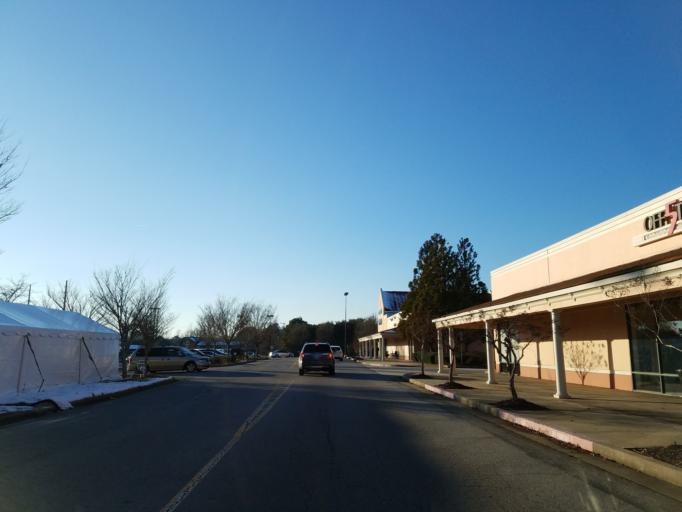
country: US
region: Georgia
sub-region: Dawson County
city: Dawsonville
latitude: 34.3546
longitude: -84.0484
